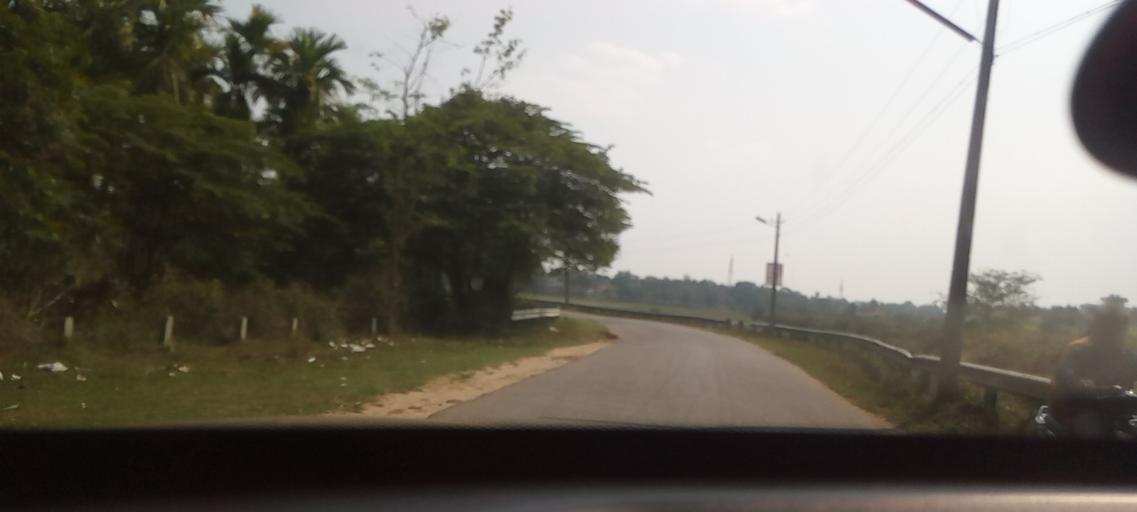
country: IN
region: Karnataka
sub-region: Hassan
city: Belur
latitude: 13.1718
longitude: 75.8598
